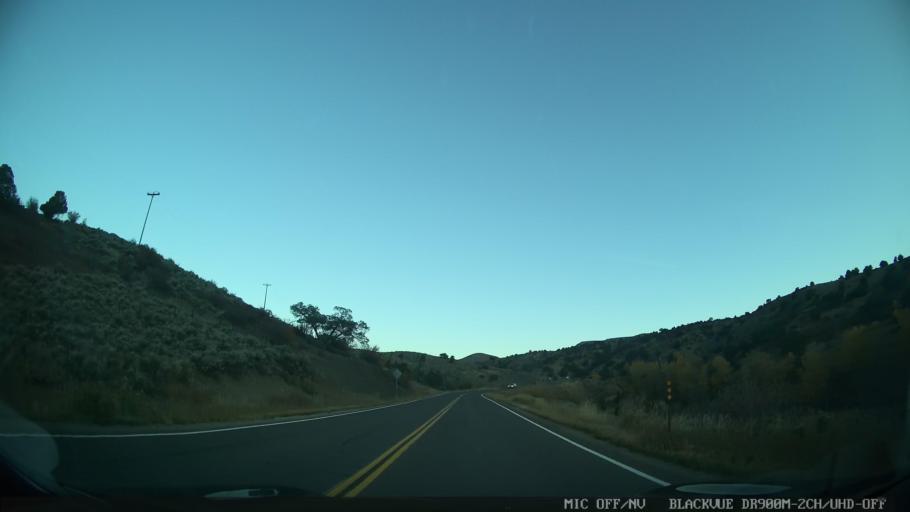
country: US
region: Colorado
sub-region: Eagle County
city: Edwards
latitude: 39.7568
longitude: -106.6718
